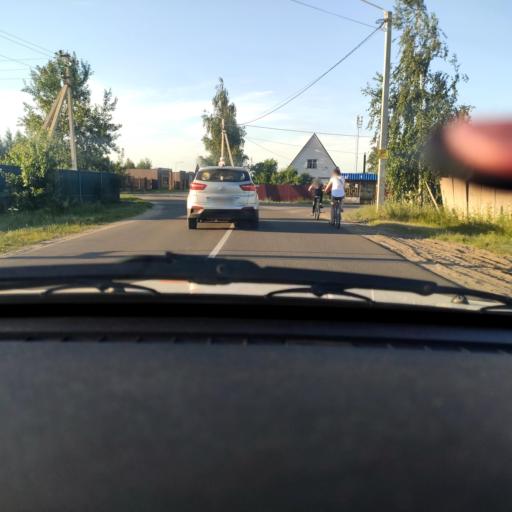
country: RU
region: Voronezj
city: Ramon'
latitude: 51.8912
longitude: 39.2535
